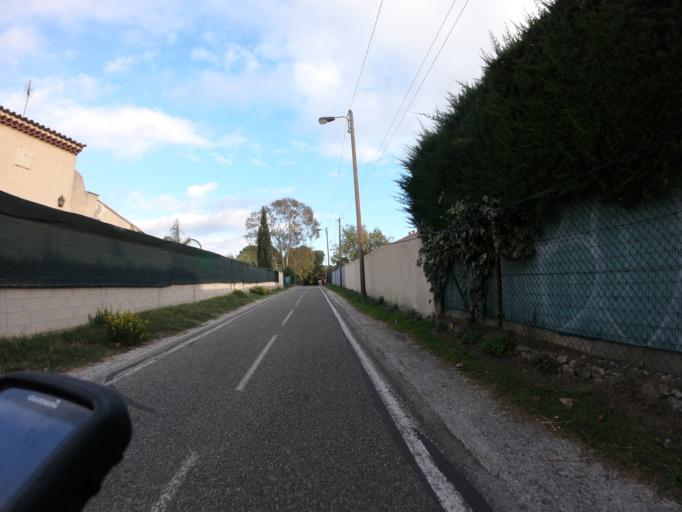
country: FR
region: Provence-Alpes-Cote d'Azur
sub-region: Departement du Var
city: La Garde
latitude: 43.1105
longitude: 5.9969
